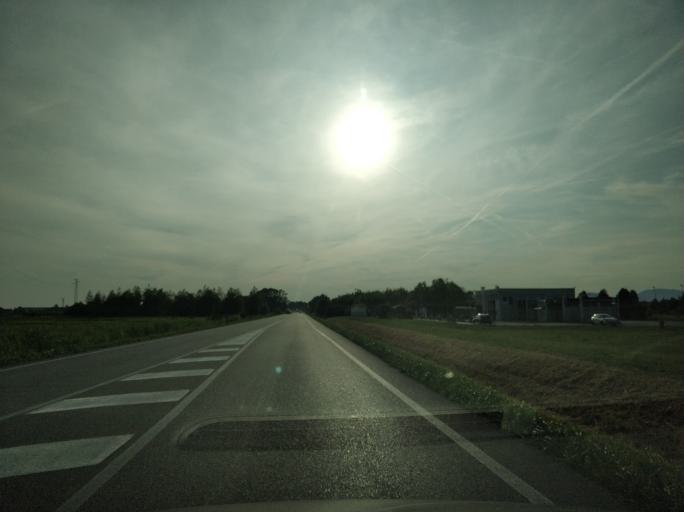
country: IT
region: Veneto
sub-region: Provincia di Padova
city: Tribano
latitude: 45.2149
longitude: 11.8581
